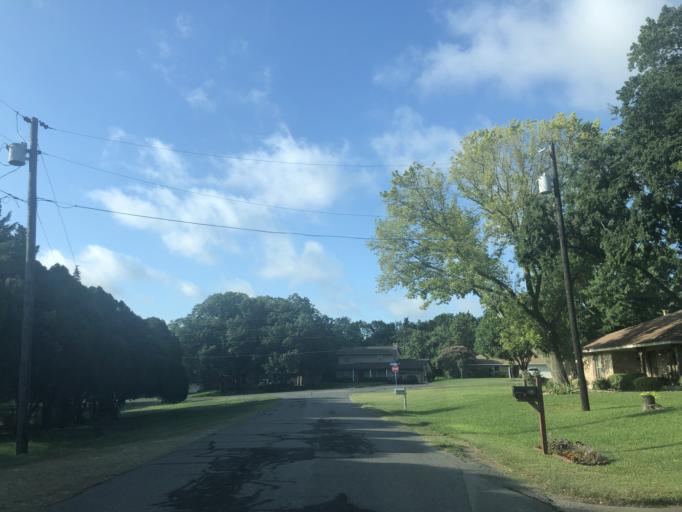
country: US
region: Texas
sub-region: Dallas County
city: Duncanville
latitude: 32.6689
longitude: -96.9132
